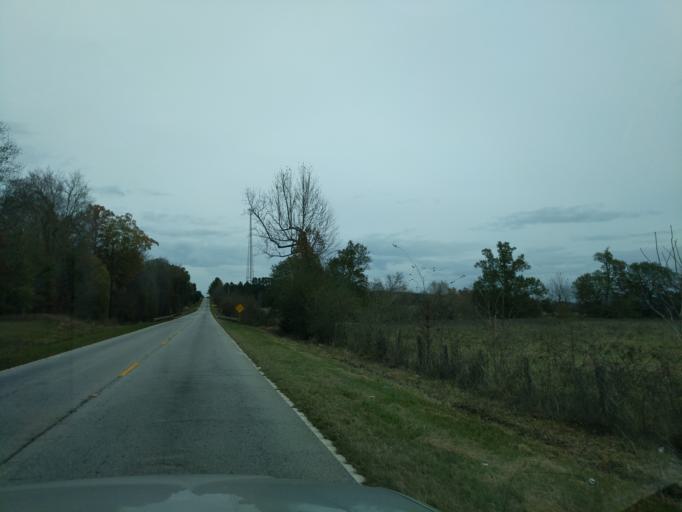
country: US
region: South Carolina
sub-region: Saluda County
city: Saluda
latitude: 34.0593
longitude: -81.7639
